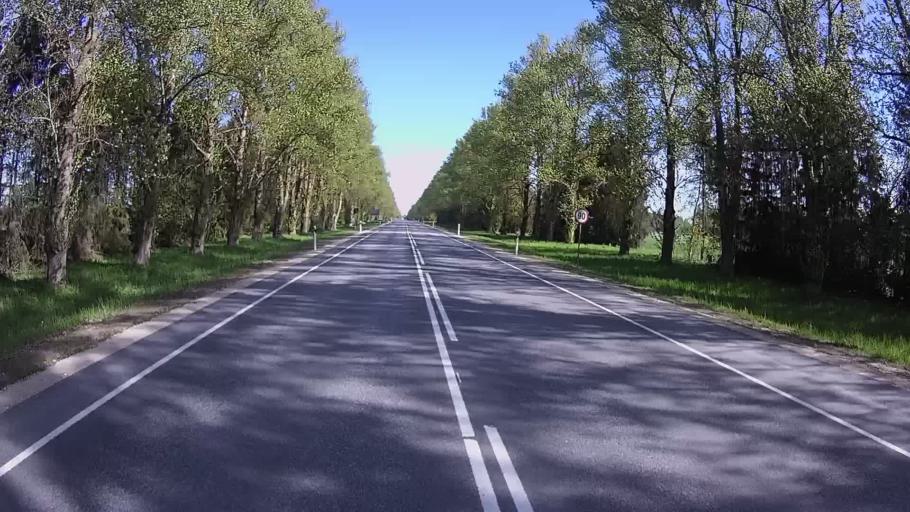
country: EE
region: Polvamaa
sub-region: Polva linn
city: Polva
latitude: 58.2854
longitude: 27.0020
